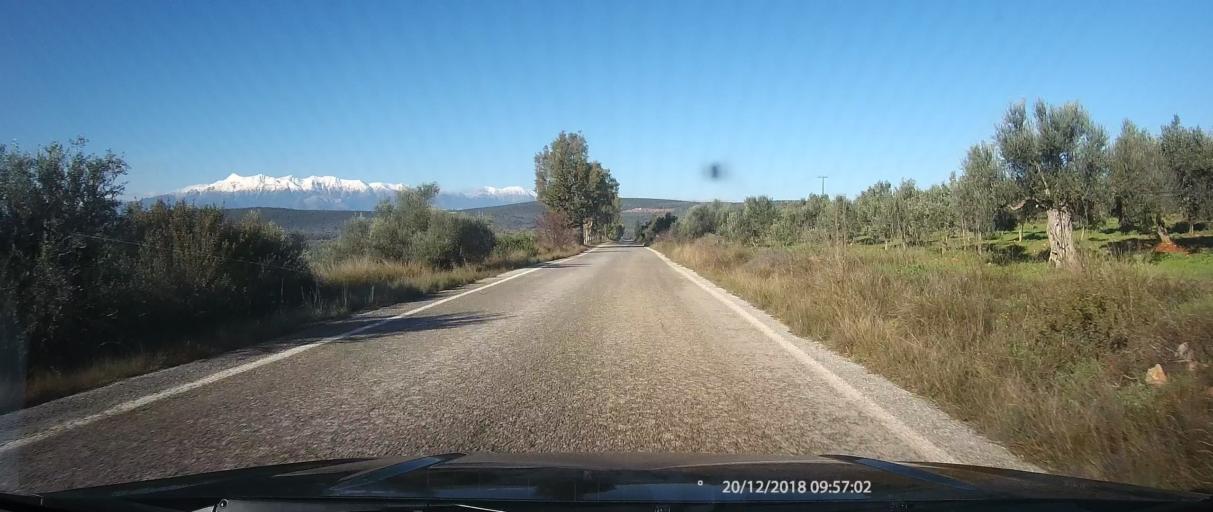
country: GR
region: Peloponnese
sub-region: Nomos Lakonias
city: Yerakion
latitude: 37.0211
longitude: 22.6034
